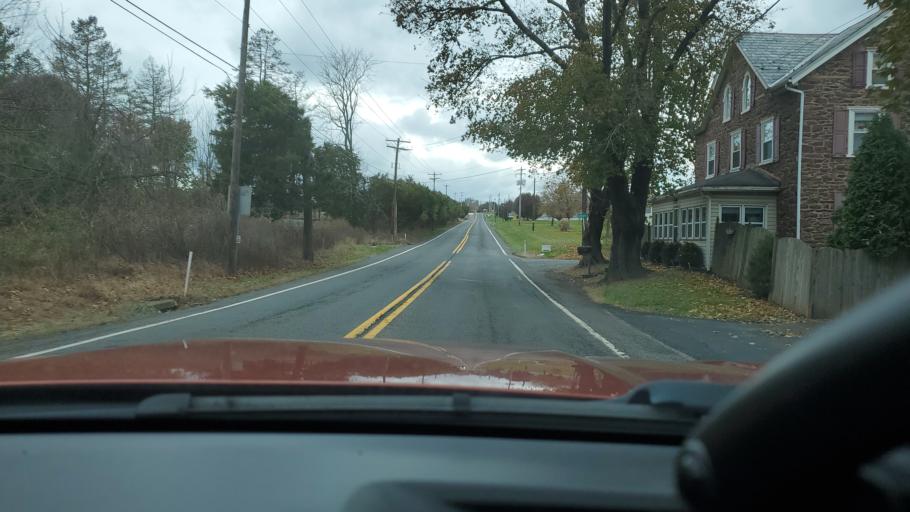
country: US
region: Pennsylvania
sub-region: Montgomery County
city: Spring Mount
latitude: 40.2814
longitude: -75.5005
